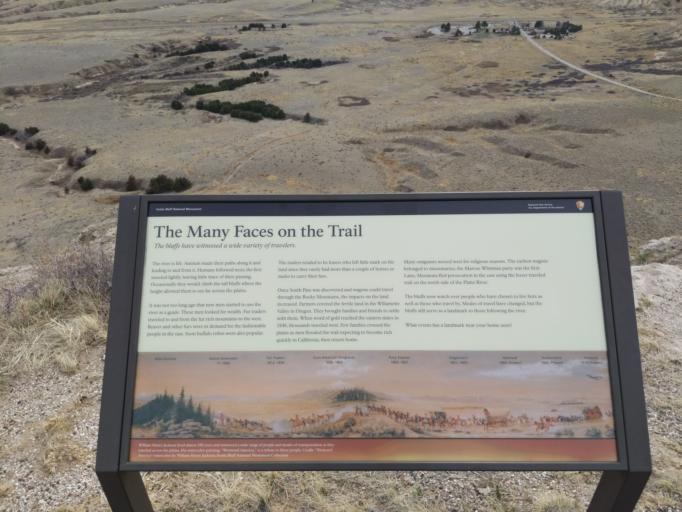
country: US
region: Nebraska
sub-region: Scotts Bluff County
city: Terrytown
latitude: 41.8348
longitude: -103.6997
